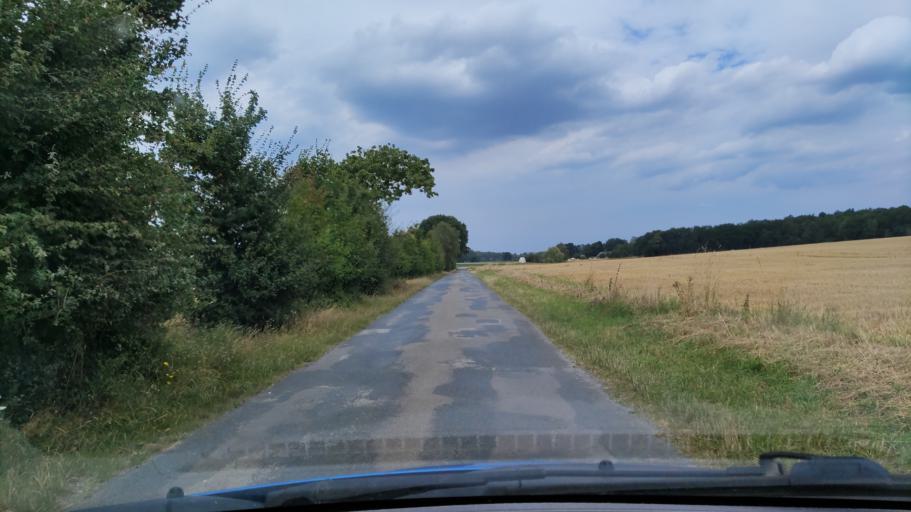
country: DE
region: Lower Saxony
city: Schnega
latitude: 52.9326
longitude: 10.8801
